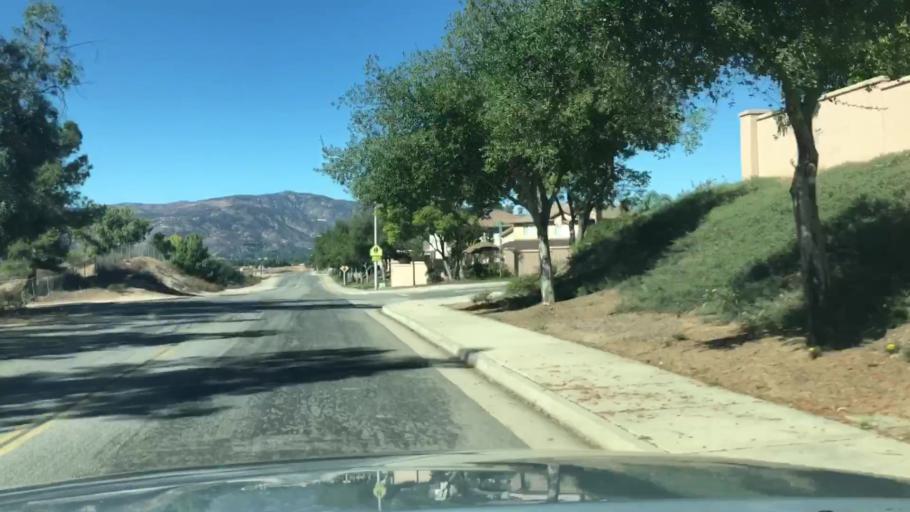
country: US
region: California
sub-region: Riverside County
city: Wildomar
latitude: 33.6052
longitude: -117.2379
